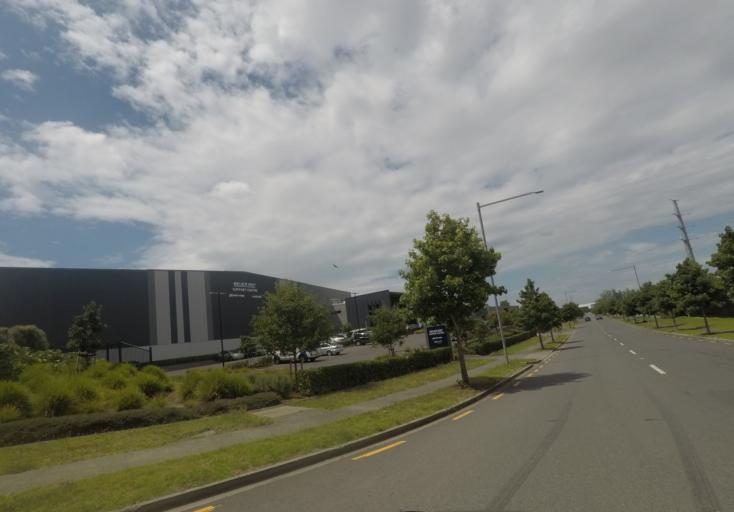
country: NZ
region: Auckland
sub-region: Auckland
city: Manukau City
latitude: -36.9442
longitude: 174.8716
